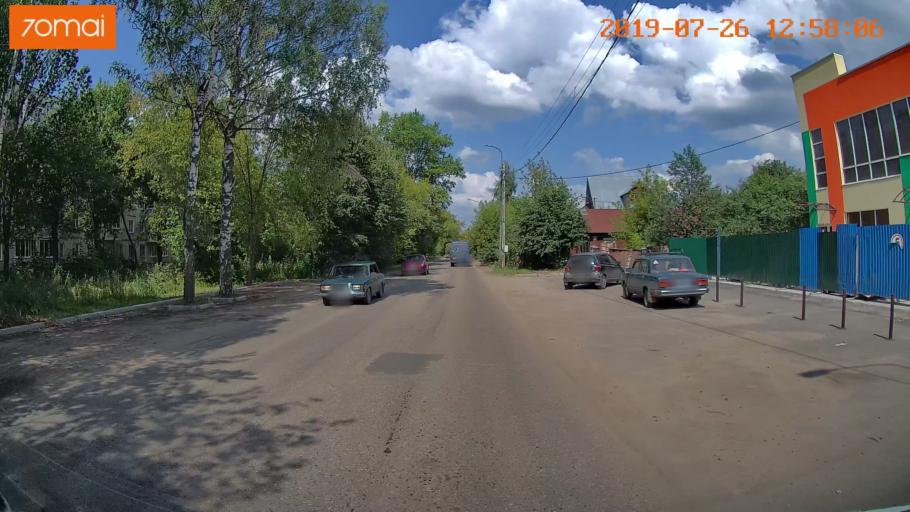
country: RU
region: Ivanovo
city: Bogorodskoye
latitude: 57.0222
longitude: 41.0208
